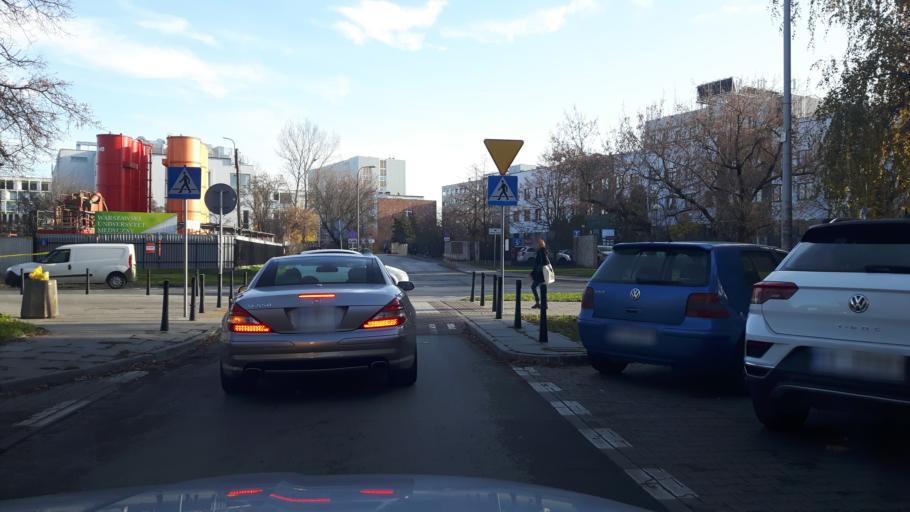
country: PL
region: Masovian Voivodeship
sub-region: Warszawa
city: Ochota
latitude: 52.2081
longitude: 20.9782
